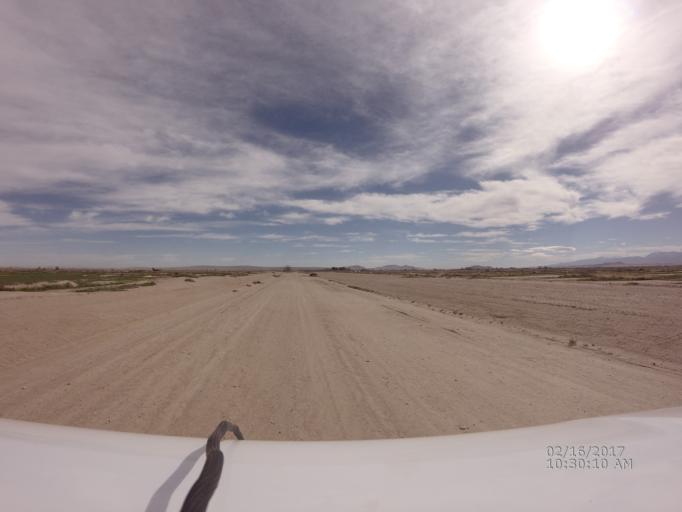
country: US
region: California
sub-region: Los Angeles County
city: Lancaster
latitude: 34.7270
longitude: -117.9664
